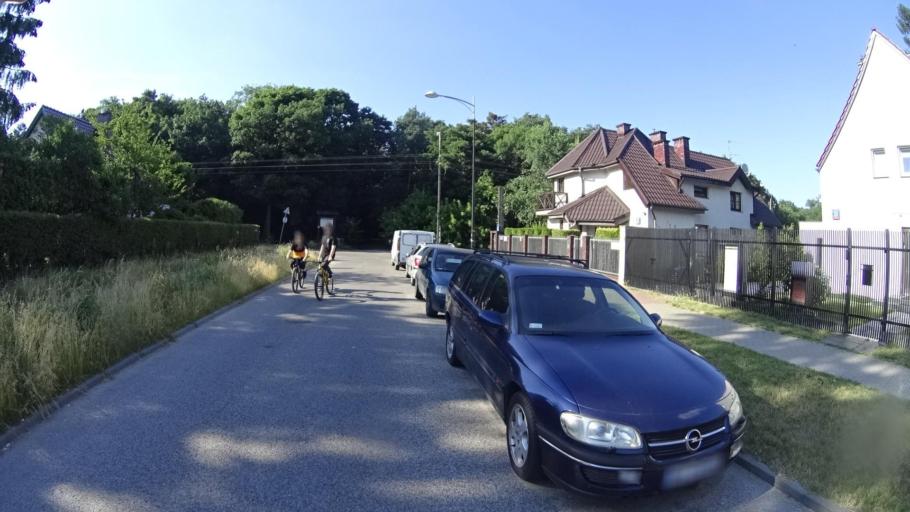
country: PL
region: Masovian Voivodeship
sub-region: Warszawa
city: Bemowo
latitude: 52.2482
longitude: 20.9474
